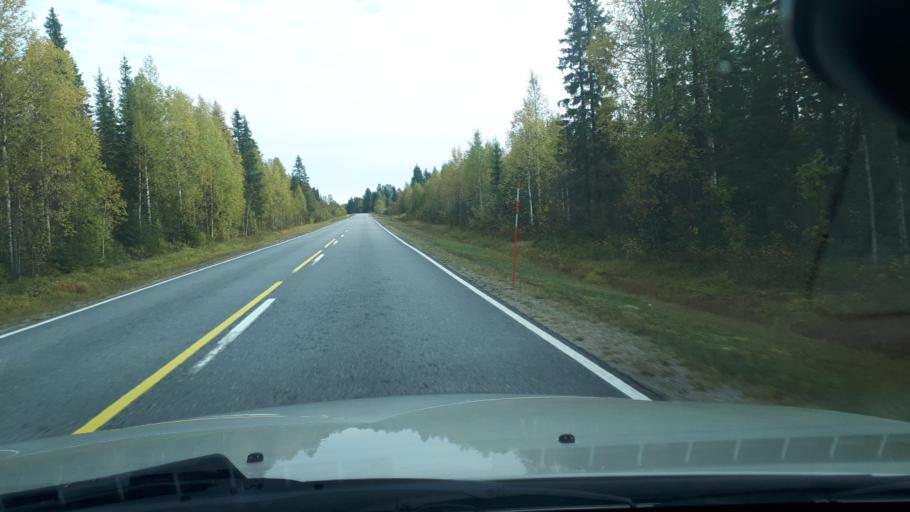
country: FI
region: Lapland
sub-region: Rovaniemi
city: Rovaniemi
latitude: 65.9526
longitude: 25.9191
